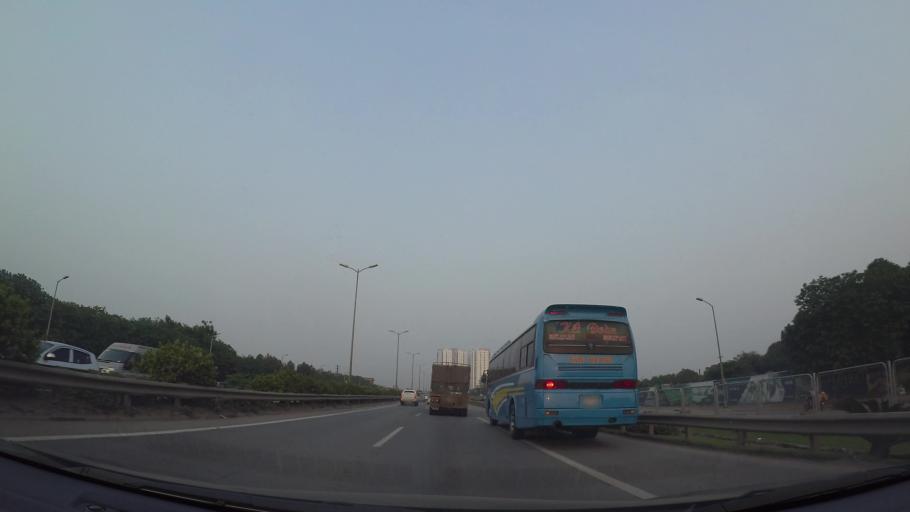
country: VN
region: Ha Noi
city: Van Dien
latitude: 20.9646
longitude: 105.8569
